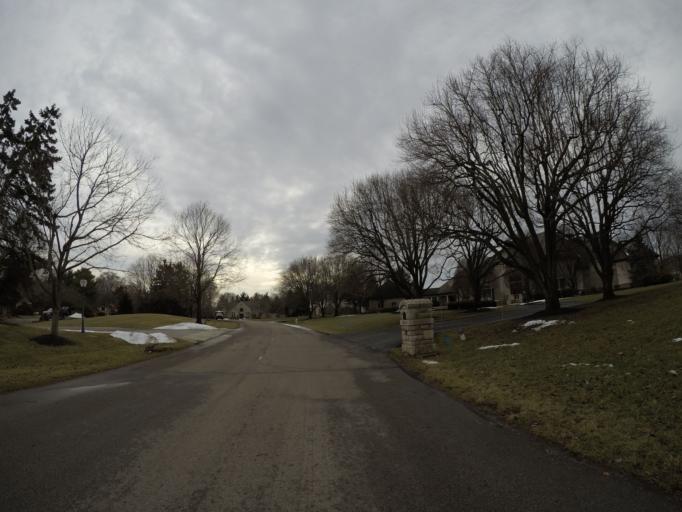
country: US
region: Ohio
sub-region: Franklin County
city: Dublin
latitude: 40.0564
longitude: -83.0927
